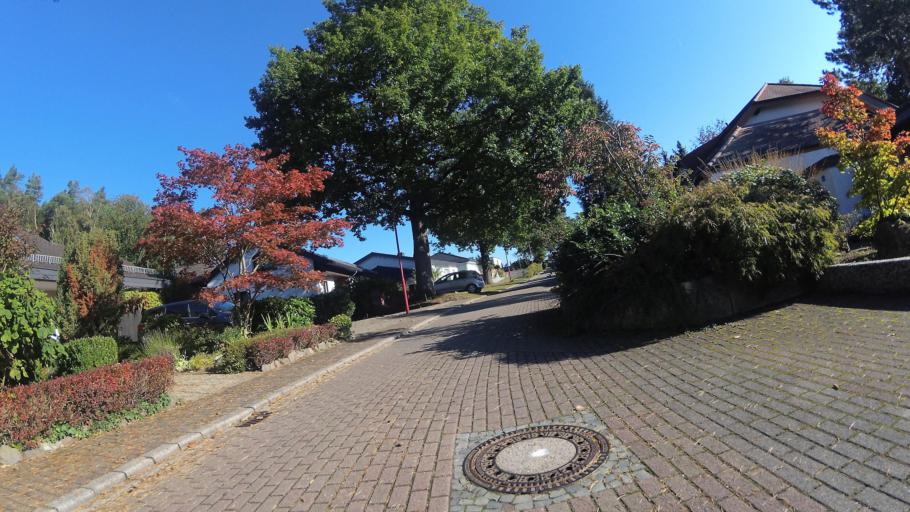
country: DE
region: Rheinland-Pfalz
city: Waldmohr
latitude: 49.3938
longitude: 7.3369
